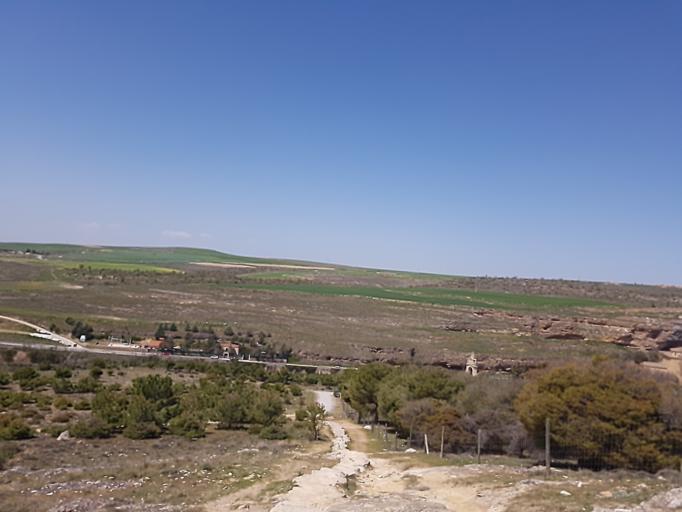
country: ES
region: Castille and Leon
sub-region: Provincia de Segovia
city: Segovia
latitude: 40.9527
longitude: -4.1351
